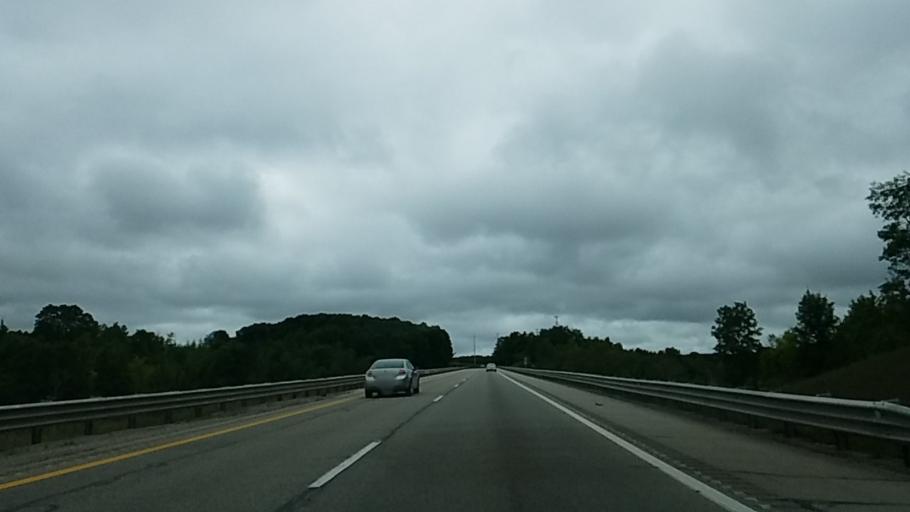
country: US
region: Michigan
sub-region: Otsego County
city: Gaylord
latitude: 45.1177
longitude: -84.6793
